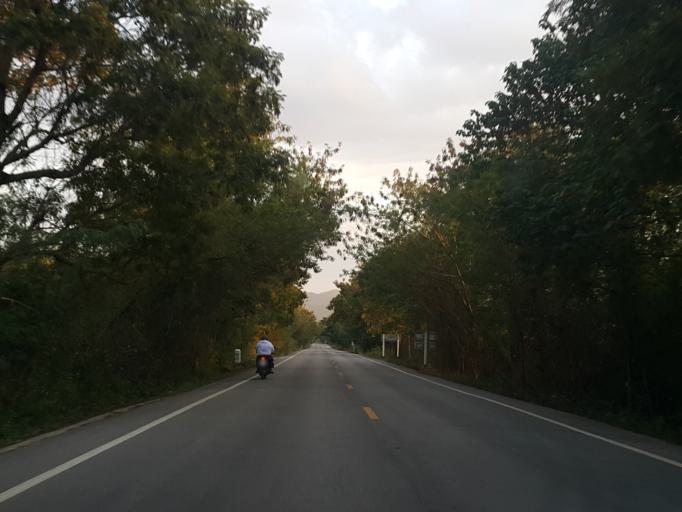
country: TH
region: Lampang
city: Mae Mo
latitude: 18.4333
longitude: 99.6420
